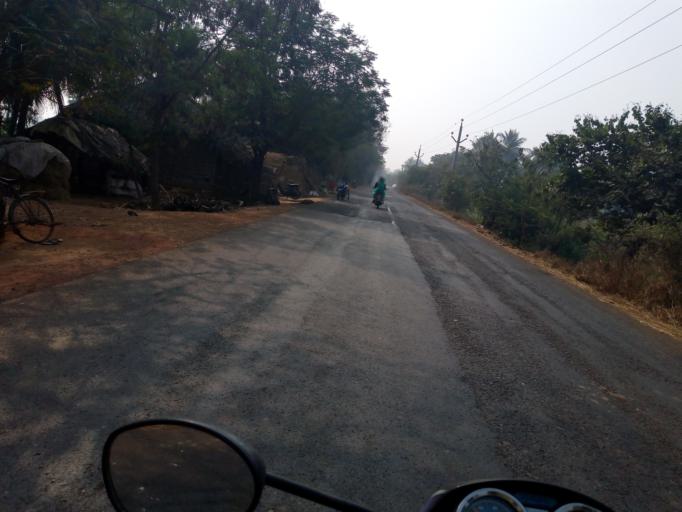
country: IN
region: Andhra Pradesh
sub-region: West Godavari
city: Tadepallegudem
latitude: 16.7872
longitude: 81.4194
